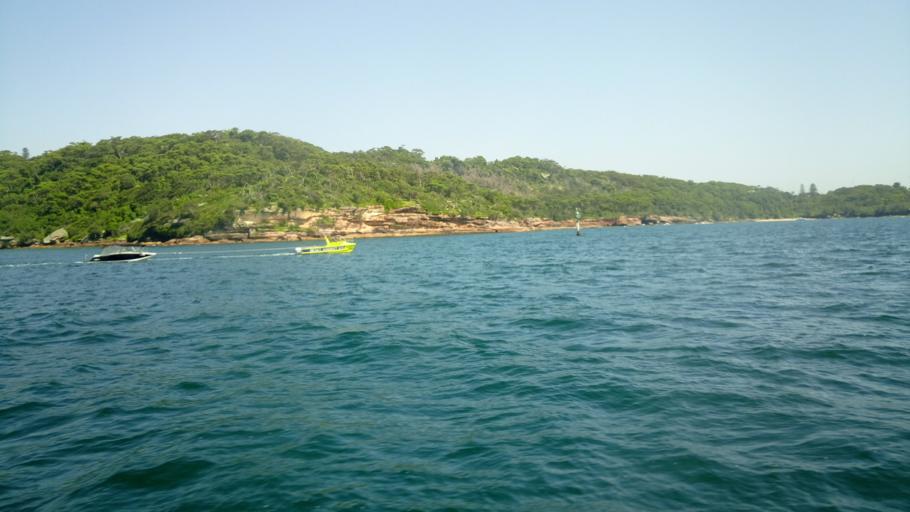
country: AU
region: New South Wales
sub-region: Mosman
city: Mosman
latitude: -33.8393
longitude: 151.2639
